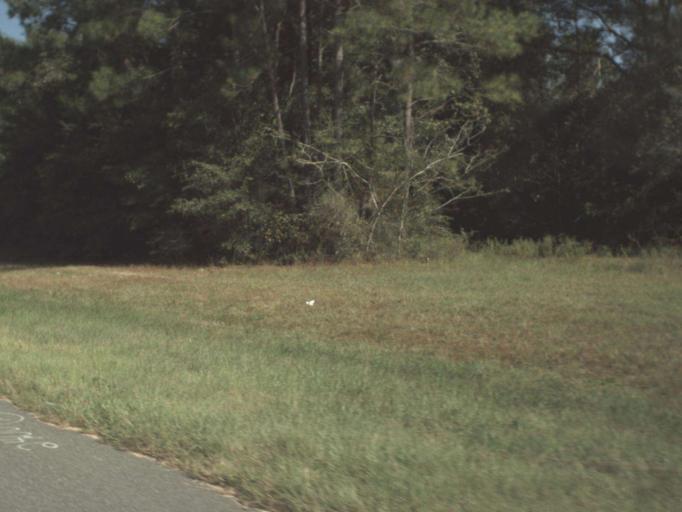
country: US
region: Florida
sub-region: Okaloosa County
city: Crestview
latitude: 30.8708
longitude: -86.5226
